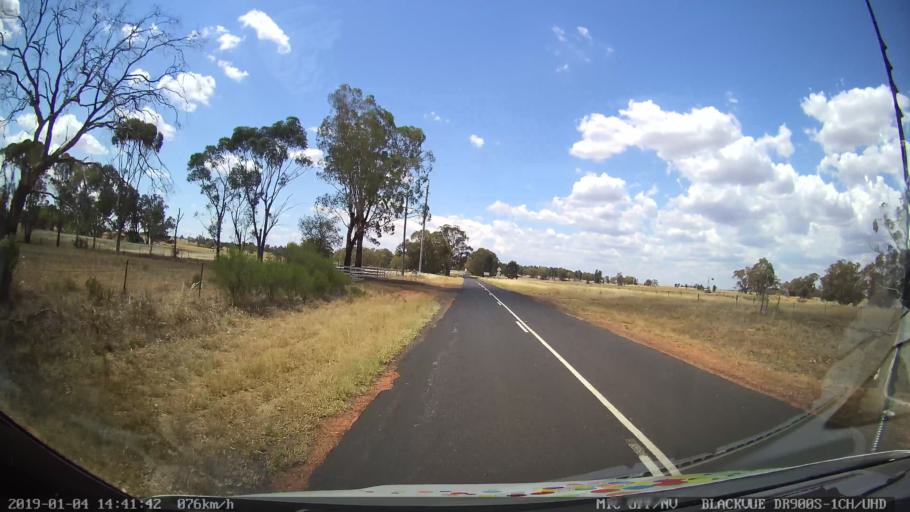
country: AU
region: New South Wales
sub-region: Dubbo Municipality
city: Dubbo
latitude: -32.1361
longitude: 148.6375
